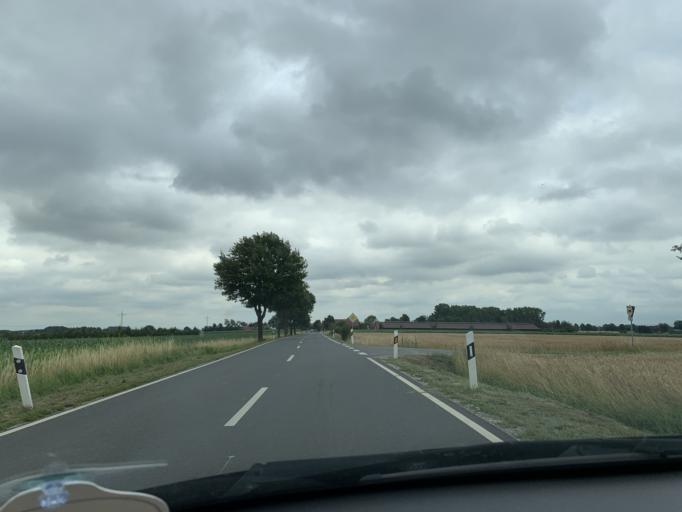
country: DE
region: North Rhine-Westphalia
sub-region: Regierungsbezirk Munster
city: Wadersloh
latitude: 51.7562
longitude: 8.2119
